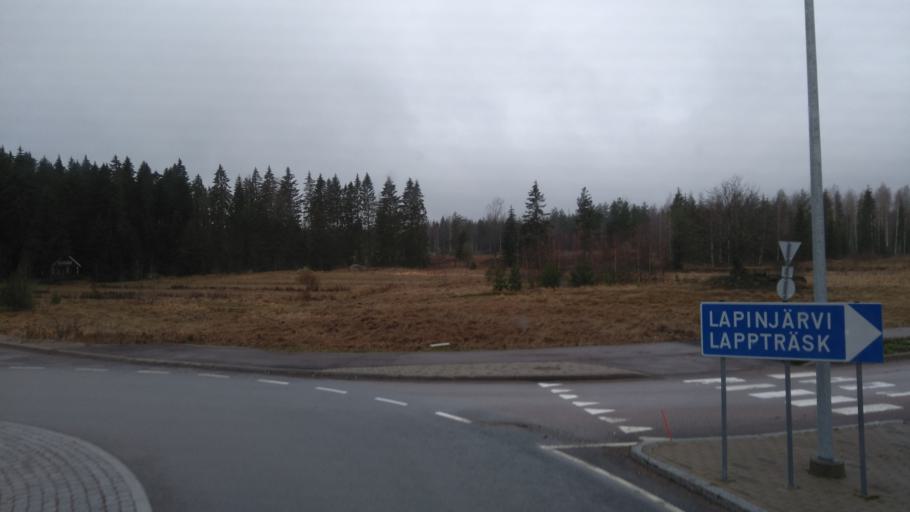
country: FI
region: Uusimaa
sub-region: Loviisa
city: Lovisa
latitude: 60.4622
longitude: 26.1922
